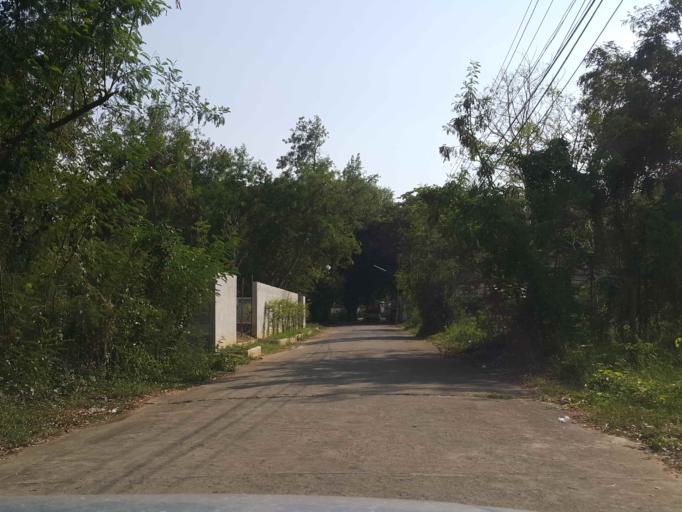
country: TH
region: Chiang Mai
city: Chiang Mai
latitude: 18.7645
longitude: 98.9943
